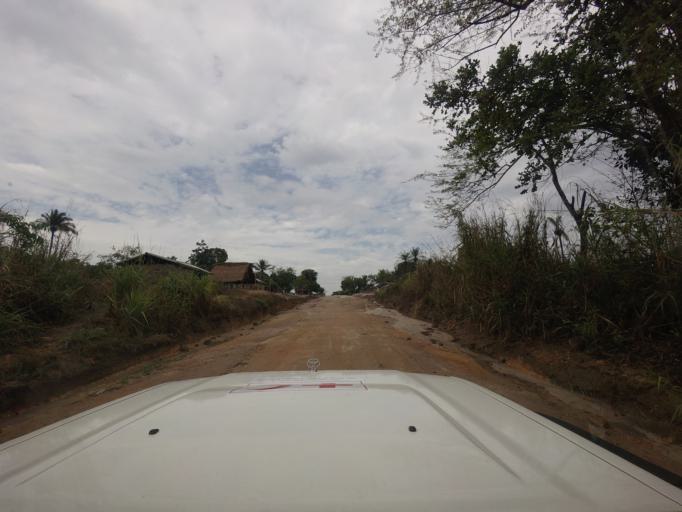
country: SL
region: Eastern Province
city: Buedu
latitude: 8.2887
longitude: -10.2198
